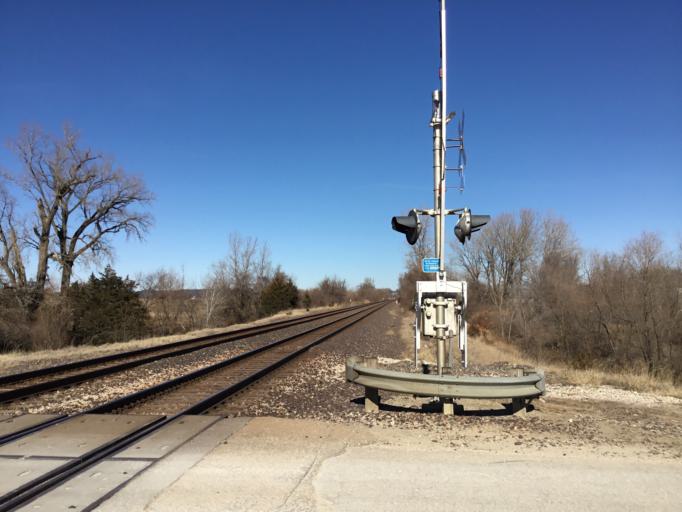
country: US
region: Kansas
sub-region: Douglas County
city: Lawrence
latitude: 39.0006
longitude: -95.2352
